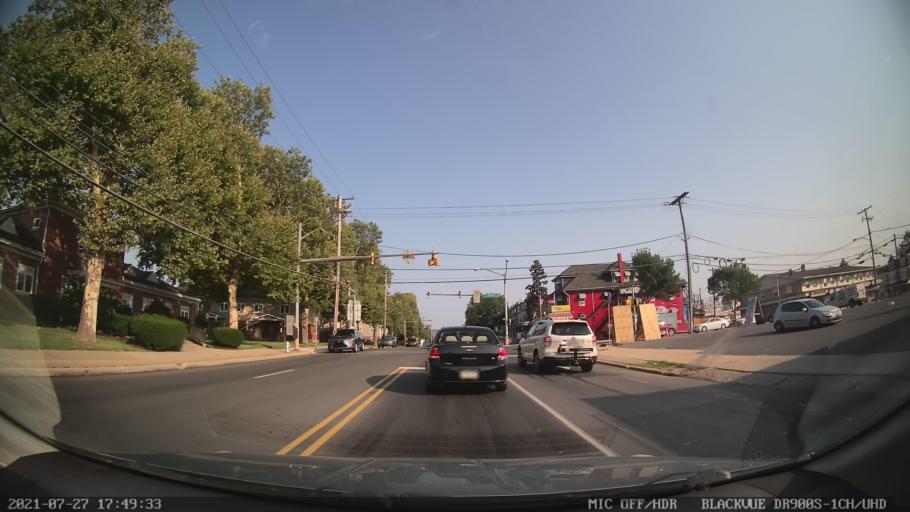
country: US
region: Pennsylvania
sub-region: Berks County
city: West Reading
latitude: 40.3549
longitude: -75.9478
